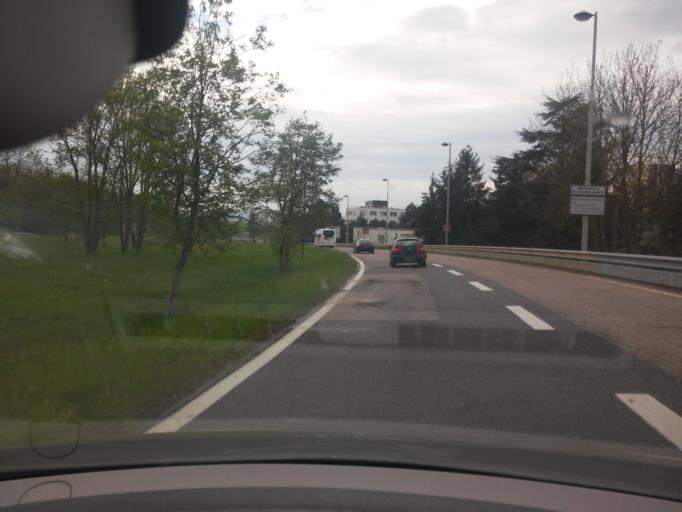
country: FR
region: Lorraine
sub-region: Departement de Meurthe-et-Moselle
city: Laxou
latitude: 48.7036
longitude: 6.1347
